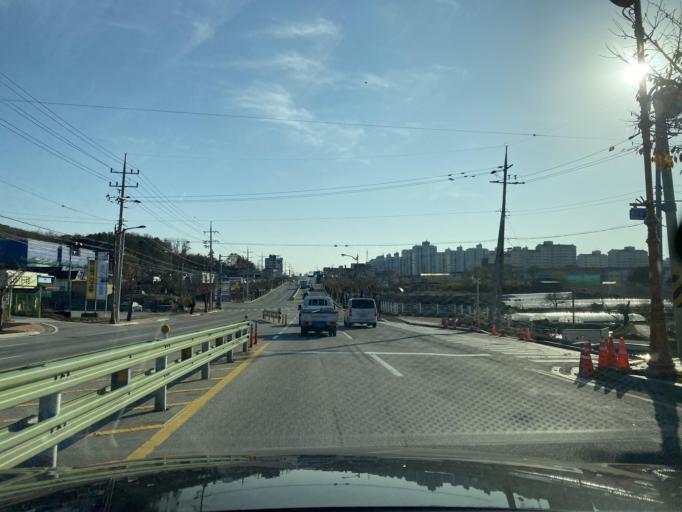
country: KR
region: Chungcheongnam-do
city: Yesan
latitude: 36.7015
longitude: 126.8383
